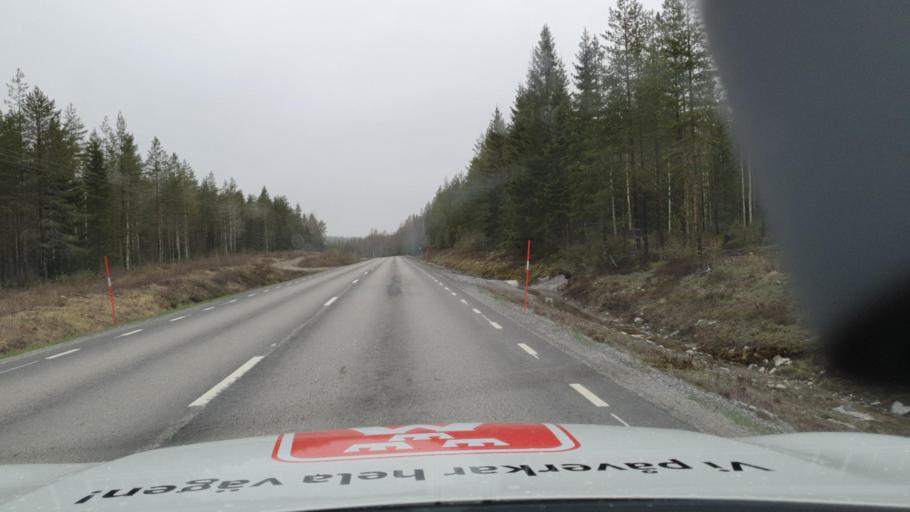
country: SE
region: Vaesterbotten
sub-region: Umea Kommun
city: Hoernefors
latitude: 63.7736
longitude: 19.9651
